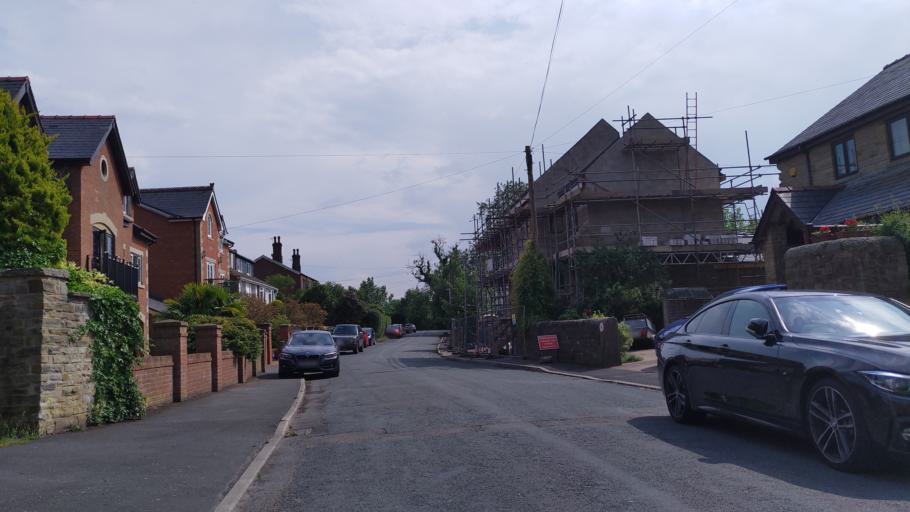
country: GB
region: England
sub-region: Lancashire
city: Chorley
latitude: 53.6797
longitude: -2.6197
